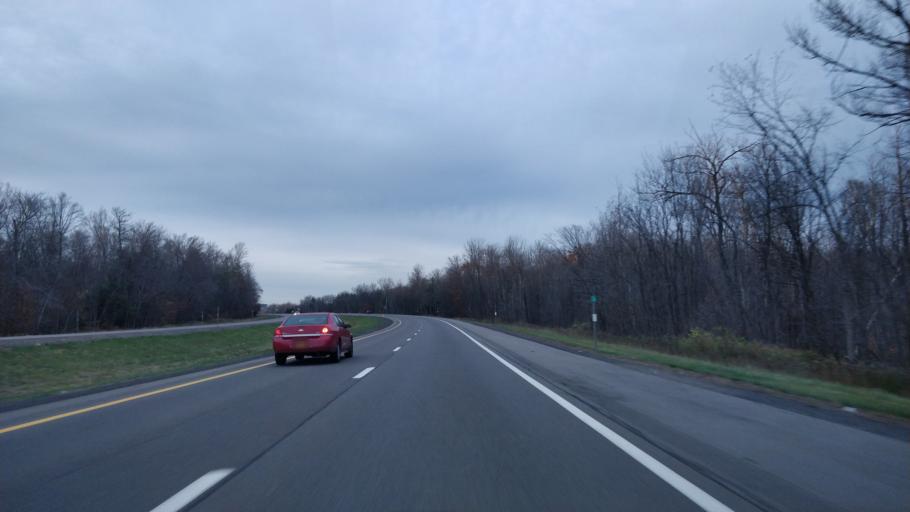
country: US
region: New York
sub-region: Oswego County
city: Central Square
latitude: 43.2974
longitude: -76.1244
